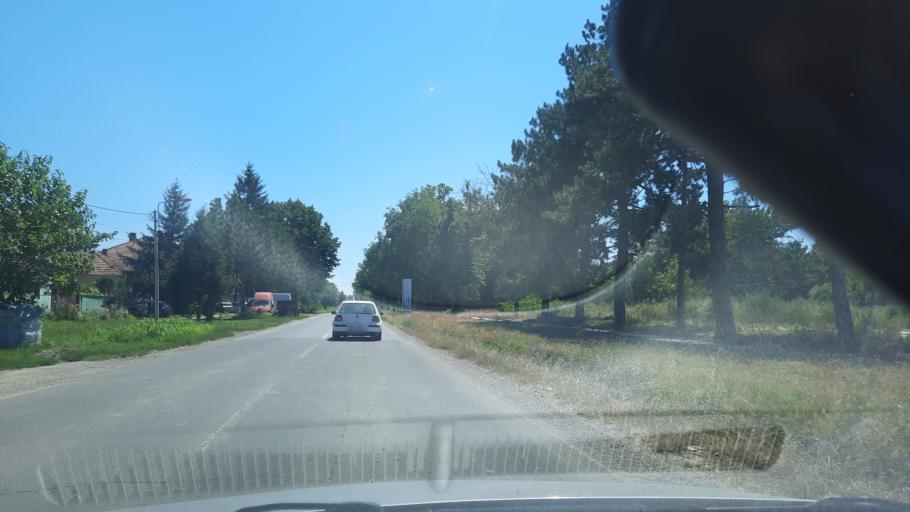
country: RS
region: Autonomna Pokrajina Vojvodina
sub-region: Juznobanatski Okrug
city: Kovin
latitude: 44.7605
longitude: 20.9857
